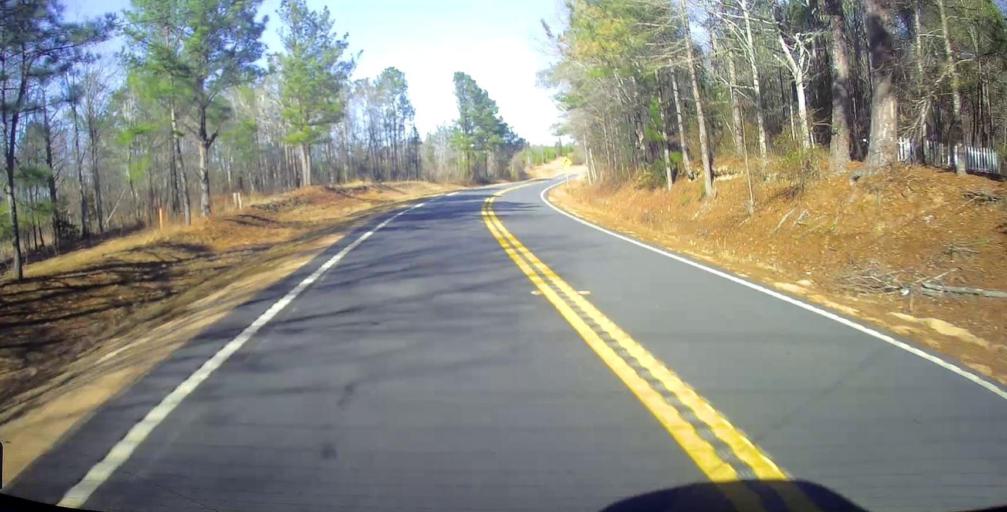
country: US
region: Georgia
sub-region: Taylor County
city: Butler
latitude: 32.6586
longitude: -84.3637
